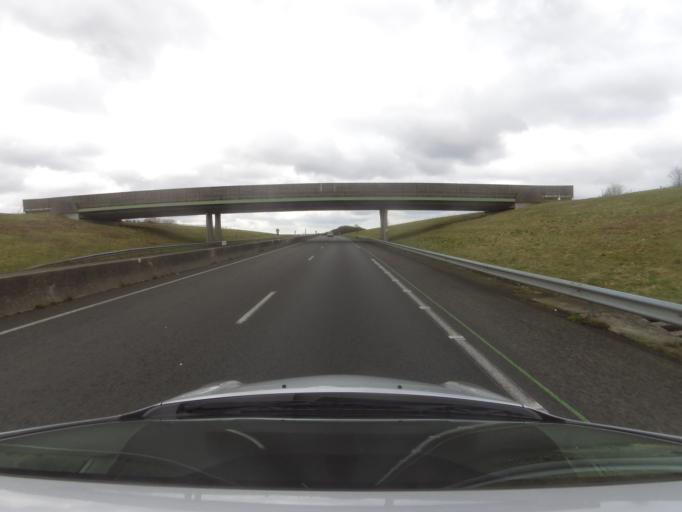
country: FR
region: Nord-Pas-de-Calais
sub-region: Departement du Pas-de-Calais
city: Neufchatel-Hardelot
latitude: 50.5953
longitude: 1.6455
